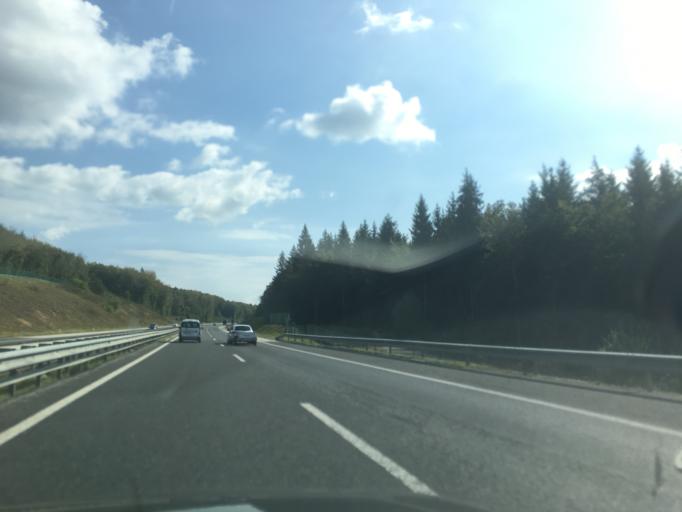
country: SI
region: Mirna Pec
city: Mirna Pec
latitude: 45.8881
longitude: 15.0658
